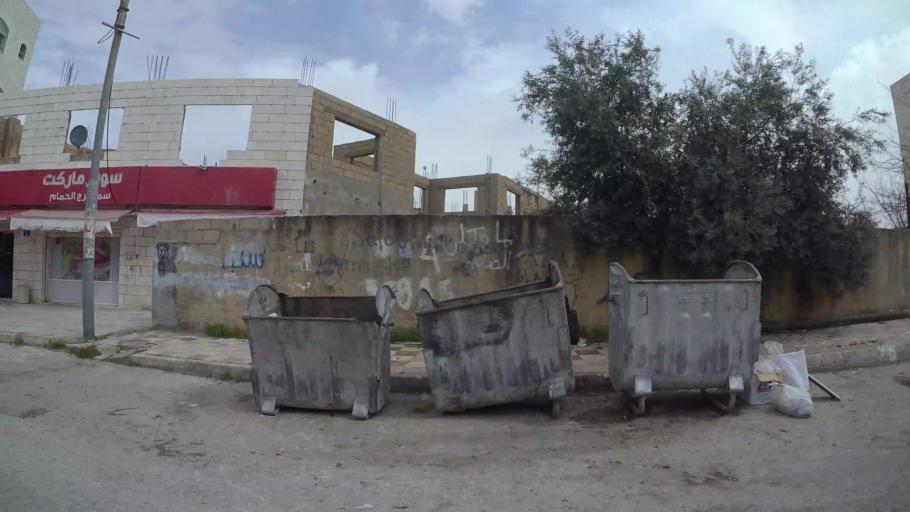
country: JO
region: Amman
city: Umm as Summaq
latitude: 31.8971
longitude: 35.8392
